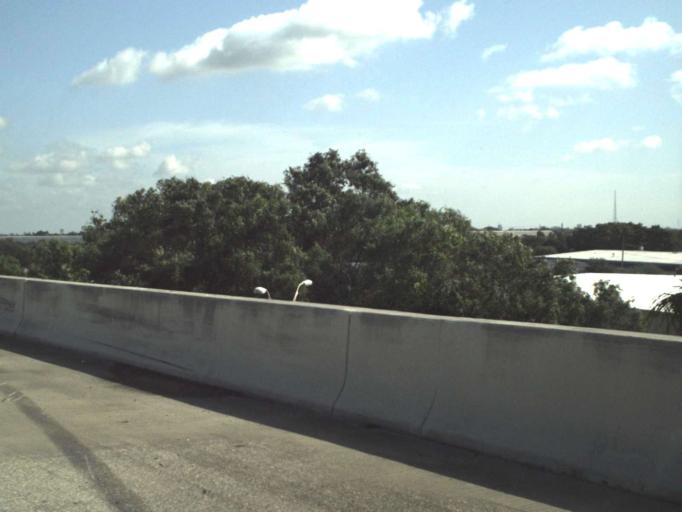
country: US
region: Florida
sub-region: Palm Beach County
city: Mangonia Park
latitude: 26.7717
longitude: -80.0958
